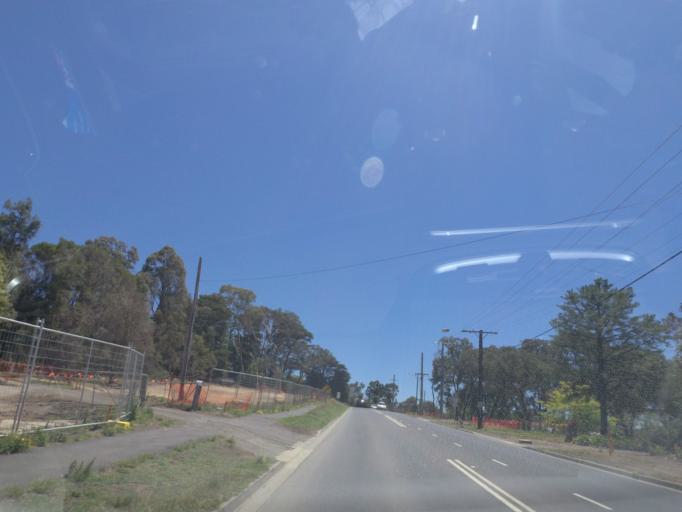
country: AU
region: Victoria
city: Plenty
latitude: -37.6651
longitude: 145.1240
